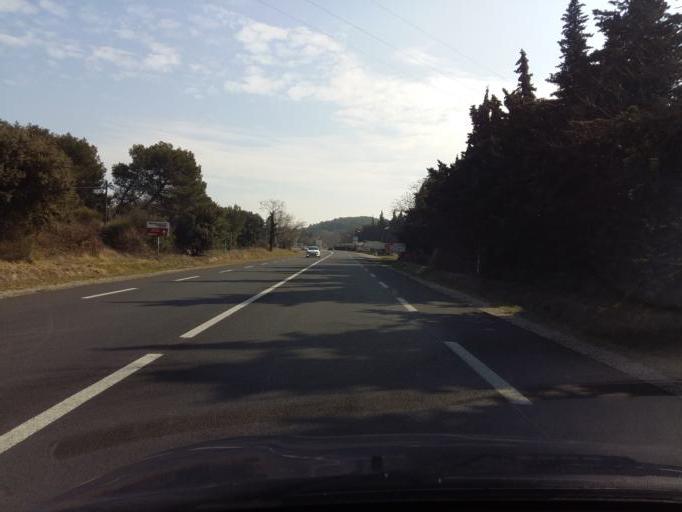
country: FR
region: Provence-Alpes-Cote d'Azur
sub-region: Departement des Bouches-du-Rhone
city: Orgon
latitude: 43.7951
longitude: 5.0157
